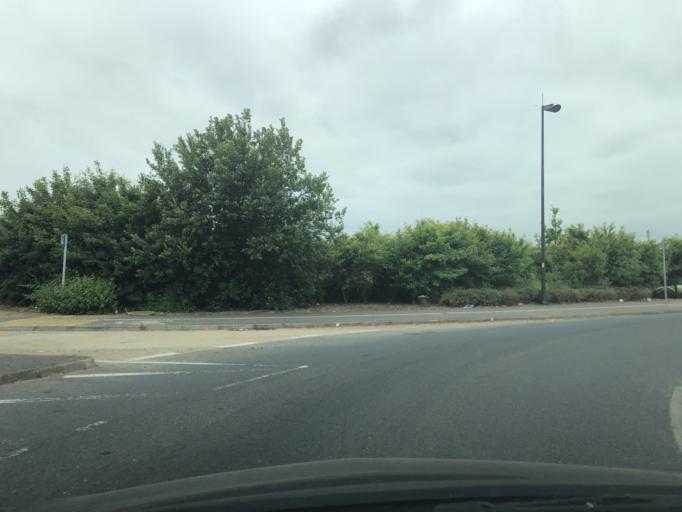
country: GB
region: England
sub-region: North Yorkshire
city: Scarborough
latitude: 54.2327
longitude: -0.4096
